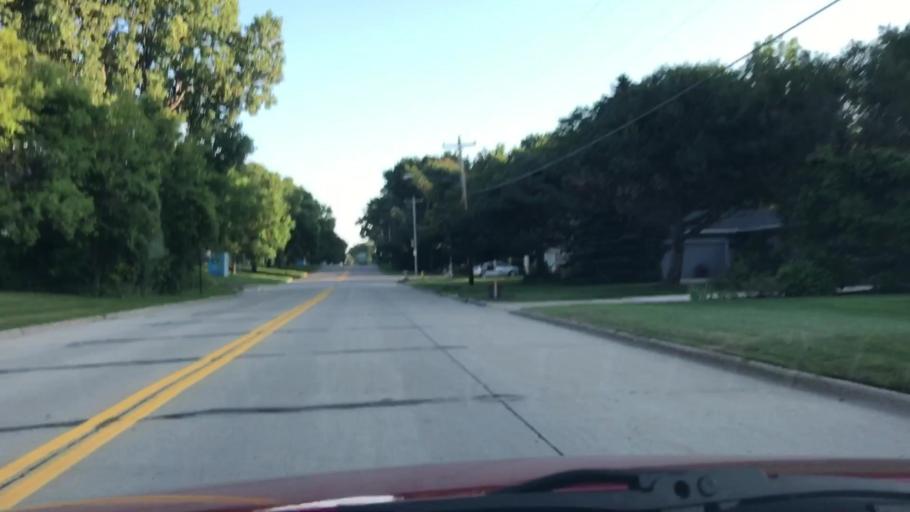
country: US
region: Wisconsin
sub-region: Brown County
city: Howard
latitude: 44.5290
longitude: -88.1096
